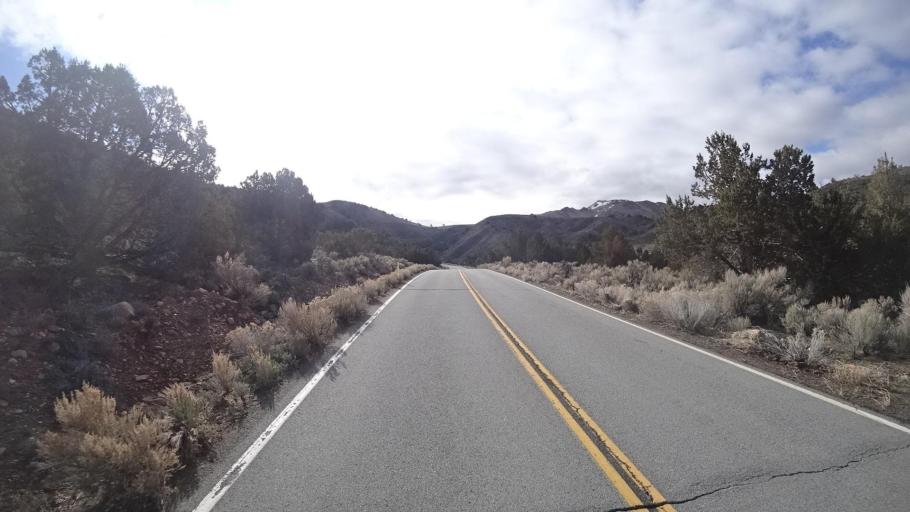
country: US
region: Nevada
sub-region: Washoe County
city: Cold Springs
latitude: 39.9060
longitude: -120.0009
